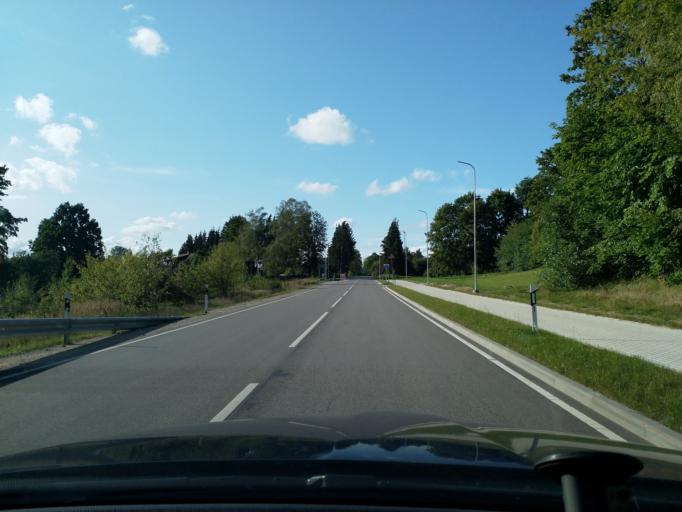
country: LV
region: Kuldigas Rajons
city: Kuldiga
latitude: 56.9691
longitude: 21.9999
